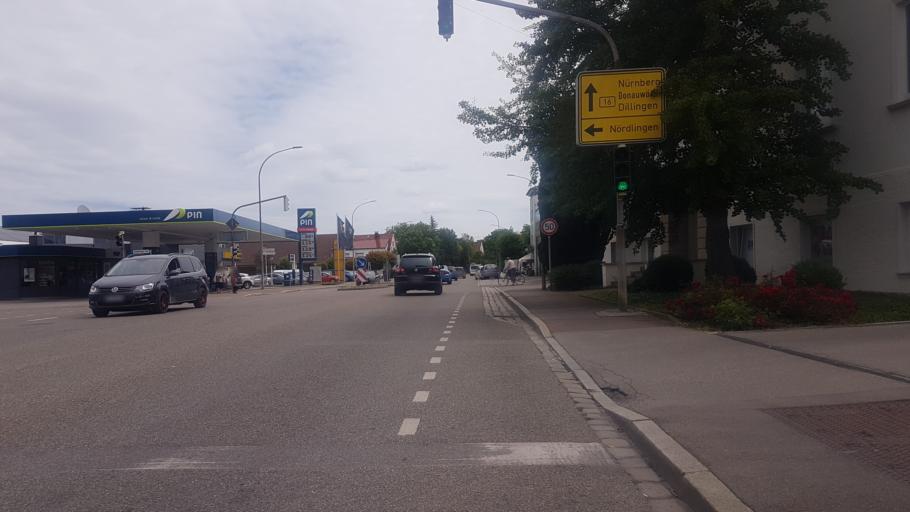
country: DE
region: Bavaria
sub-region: Swabia
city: Lauingen
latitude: 48.5732
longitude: 10.4332
